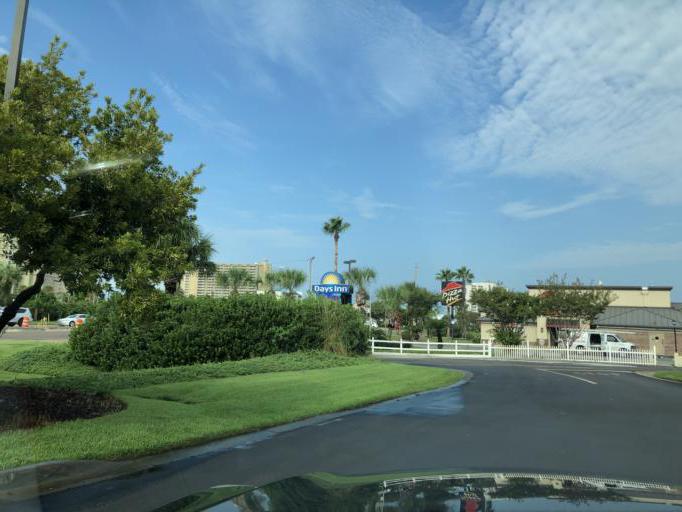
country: US
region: Florida
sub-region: Okaloosa County
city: Destin
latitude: 30.3868
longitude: -86.4692
